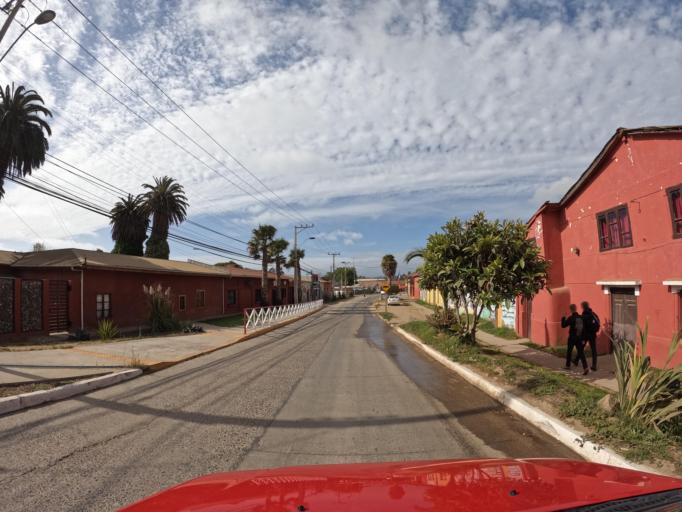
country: CL
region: O'Higgins
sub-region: Provincia de Colchagua
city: Santa Cruz
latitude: -34.3885
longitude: -72.0005
